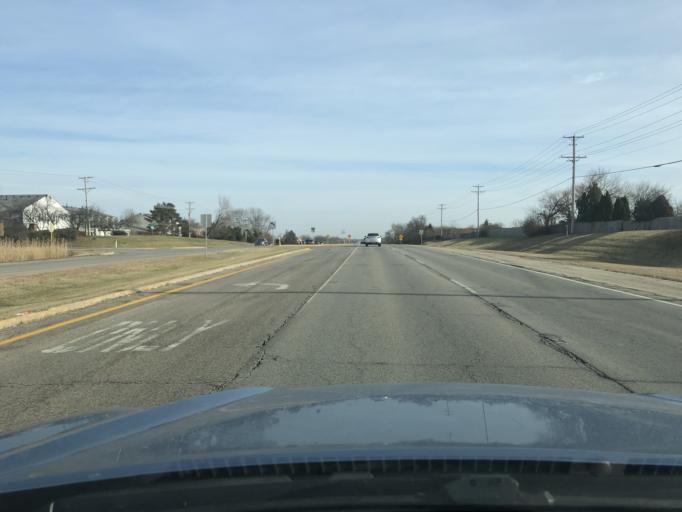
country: US
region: Illinois
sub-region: Cook County
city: South Barrington
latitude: 42.0549
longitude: -88.1291
